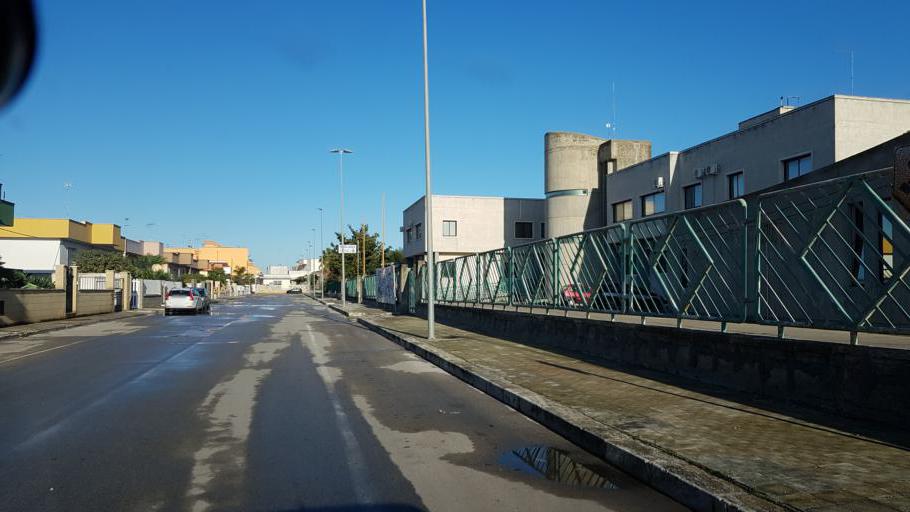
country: IT
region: Apulia
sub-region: Provincia di Brindisi
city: Torchiarolo
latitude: 40.4796
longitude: 18.0559
